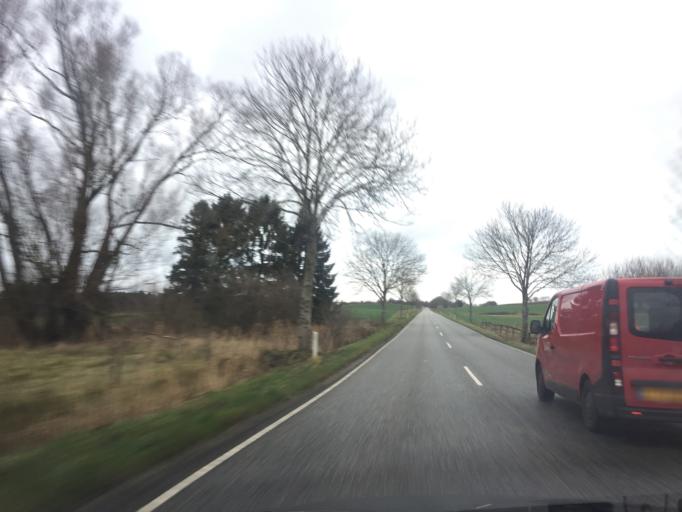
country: DK
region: Zealand
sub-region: Holbaek Kommune
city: Tollose
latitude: 55.6362
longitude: 11.7983
